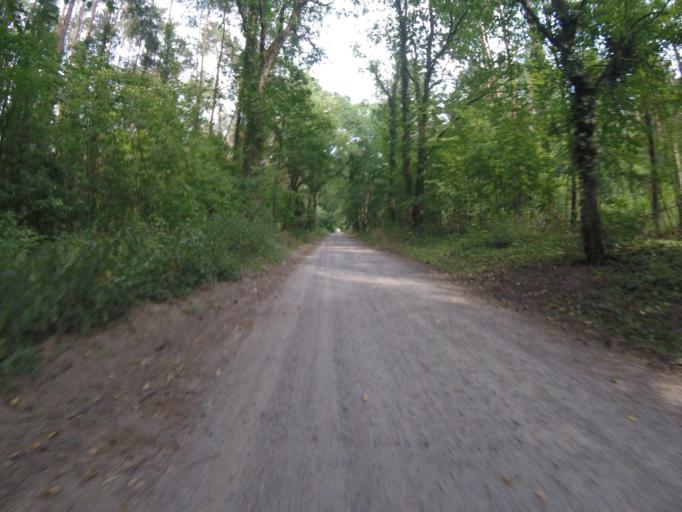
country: DE
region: Brandenburg
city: Wildau
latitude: 52.3203
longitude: 13.7229
